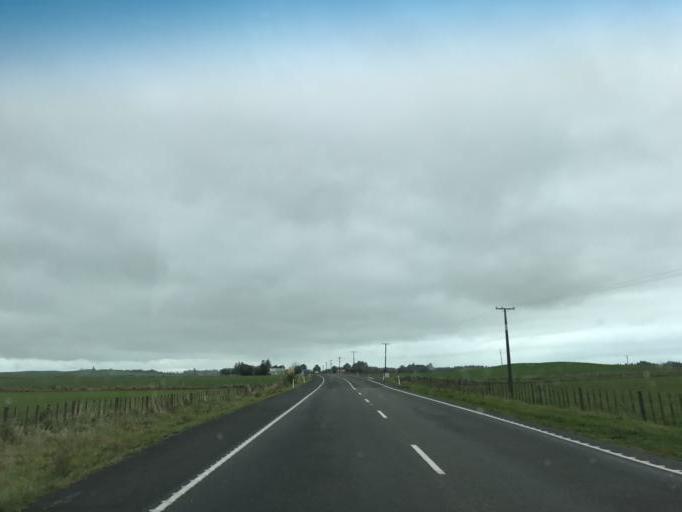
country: NZ
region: Manawatu-Wanganui
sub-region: Wanganui District
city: Wanganui
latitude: -39.8152
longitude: 174.8262
